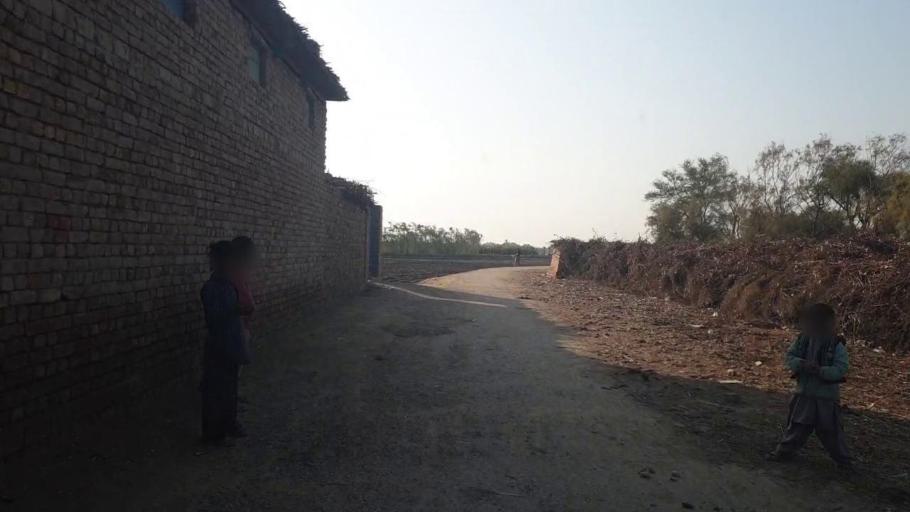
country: PK
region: Sindh
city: Bhit Shah
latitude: 25.8335
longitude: 68.5182
